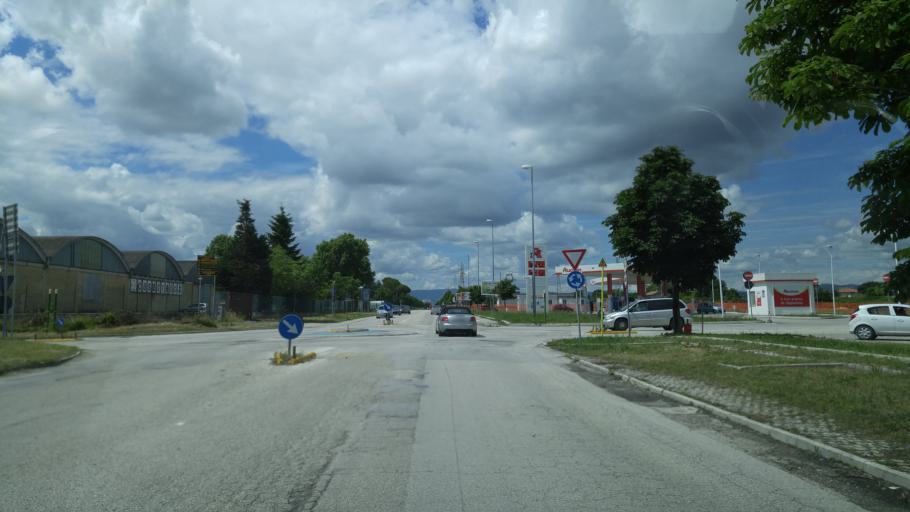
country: IT
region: The Marches
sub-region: Provincia di Pesaro e Urbino
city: Bellocchi
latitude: 43.7994
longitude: 13.0120
